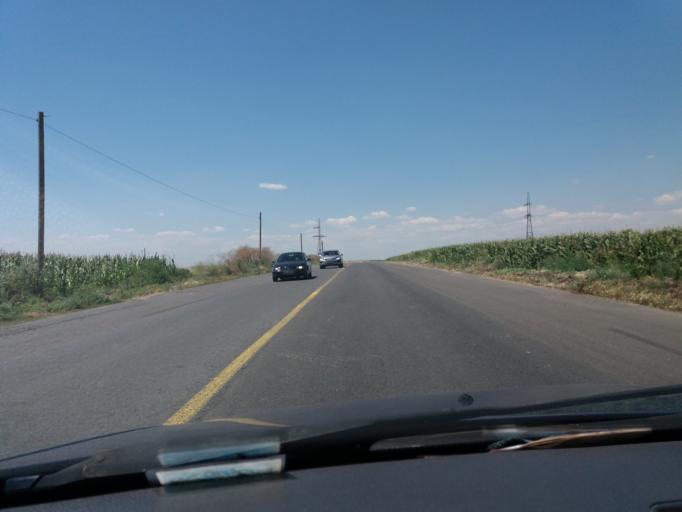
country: RO
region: Constanta
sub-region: Comuna Lumina
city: Lumina
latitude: 44.2856
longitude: 28.5828
